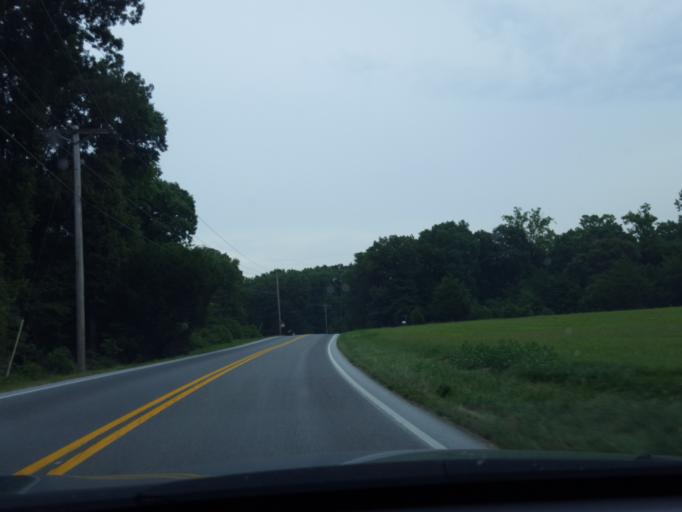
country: US
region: Maryland
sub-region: Saint Mary's County
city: Charlotte Hall
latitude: 38.4302
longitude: -76.8166
